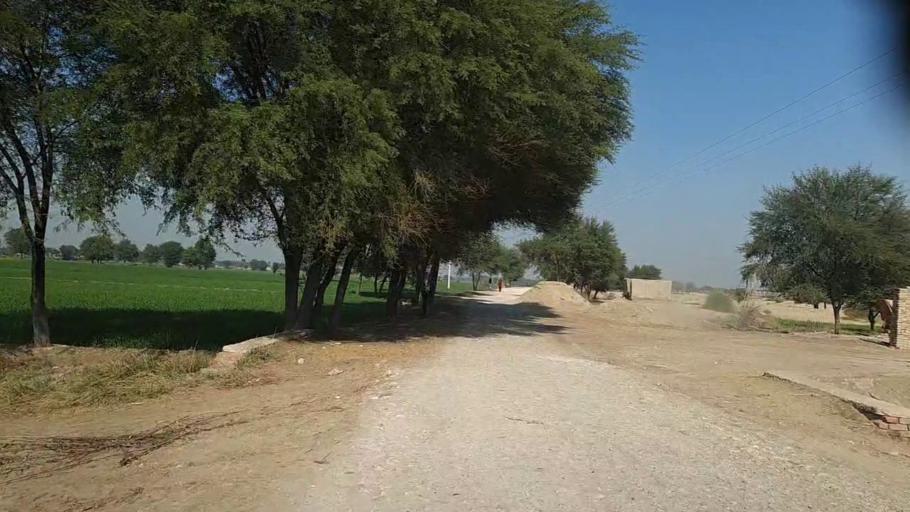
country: PK
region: Sindh
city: Khairpur
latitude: 28.0039
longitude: 69.8498
